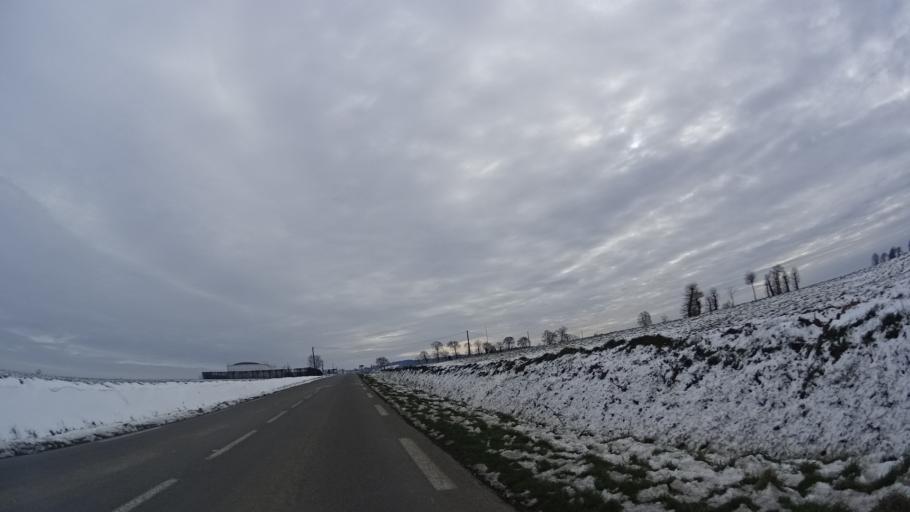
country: FR
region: Brittany
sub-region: Departement des Cotes-d'Armor
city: Plouasne
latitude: 48.3206
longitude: -1.9561
